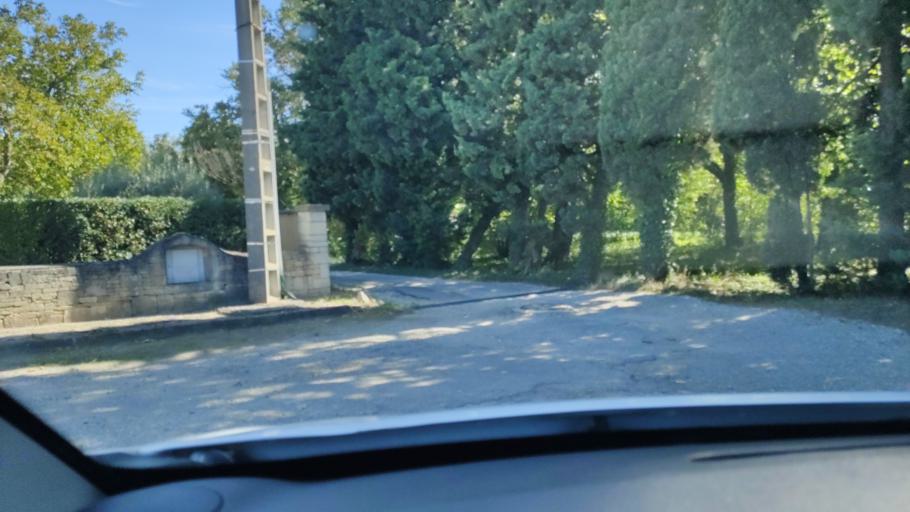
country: FR
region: Provence-Alpes-Cote d'Azur
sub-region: Departement du Vaucluse
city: Morieres-les-Avignon
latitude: 43.9473
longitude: 4.8881
